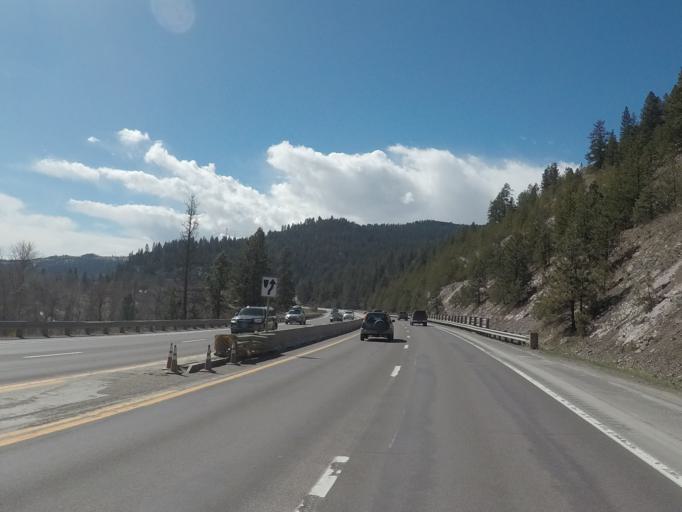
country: US
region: Montana
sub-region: Missoula County
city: Lolo
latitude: 46.8120
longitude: -114.0960
